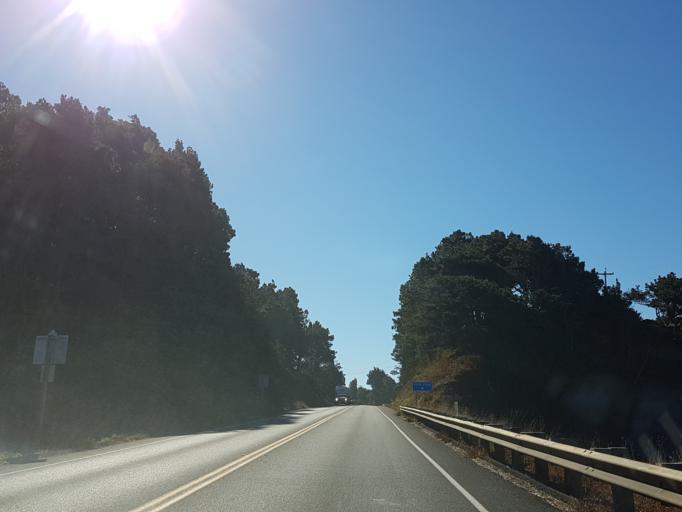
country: US
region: California
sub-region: Mendocino County
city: Fort Bragg
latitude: 39.2949
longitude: -123.7951
